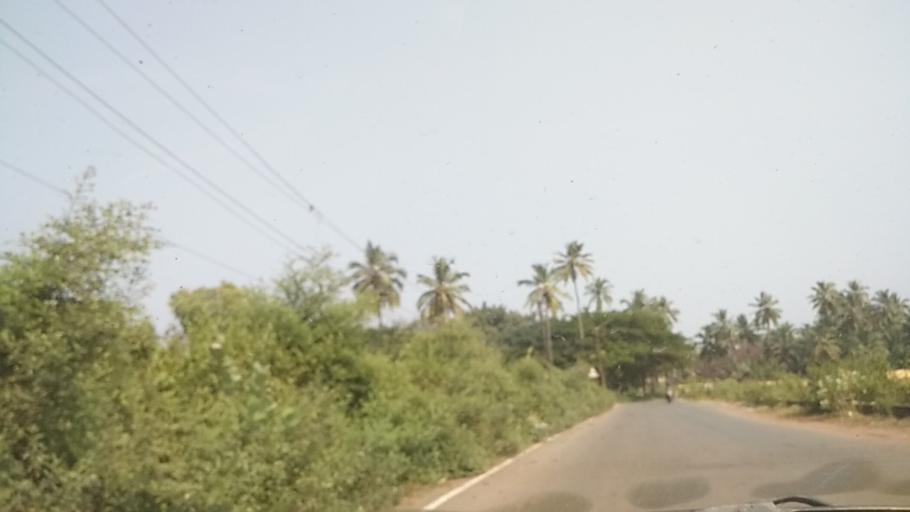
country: IN
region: Goa
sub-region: South Goa
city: Cavelossim
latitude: 15.1619
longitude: 73.9660
